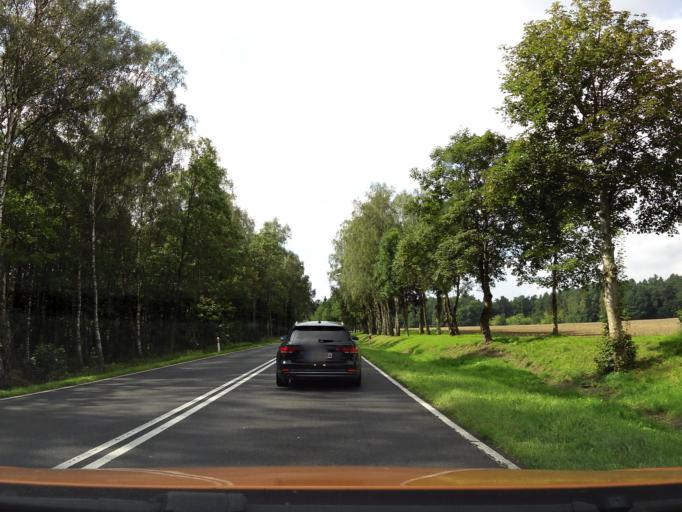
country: PL
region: West Pomeranian Voivodeship
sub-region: Powiat gryficki
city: Ploty
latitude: 53.8294
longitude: 15.2905
